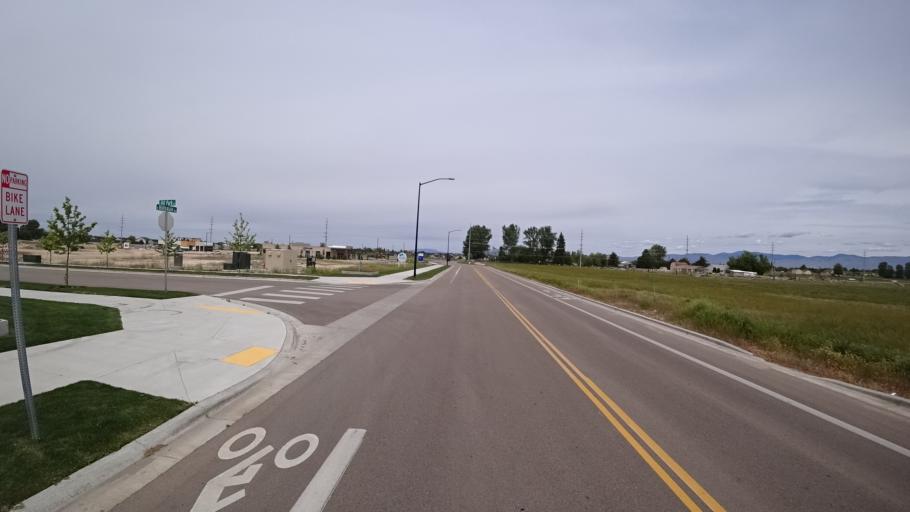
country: US
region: Idaho
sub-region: Ada County
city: Meridian
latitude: 43.5591
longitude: -116.3444
